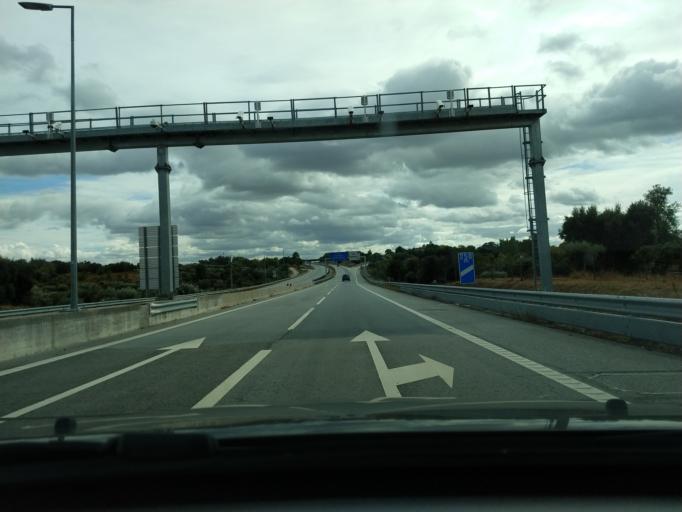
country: PT
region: Castelo Branco
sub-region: Concelho do Fundao
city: Fundao
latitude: 40.0334
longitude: -7.4686
